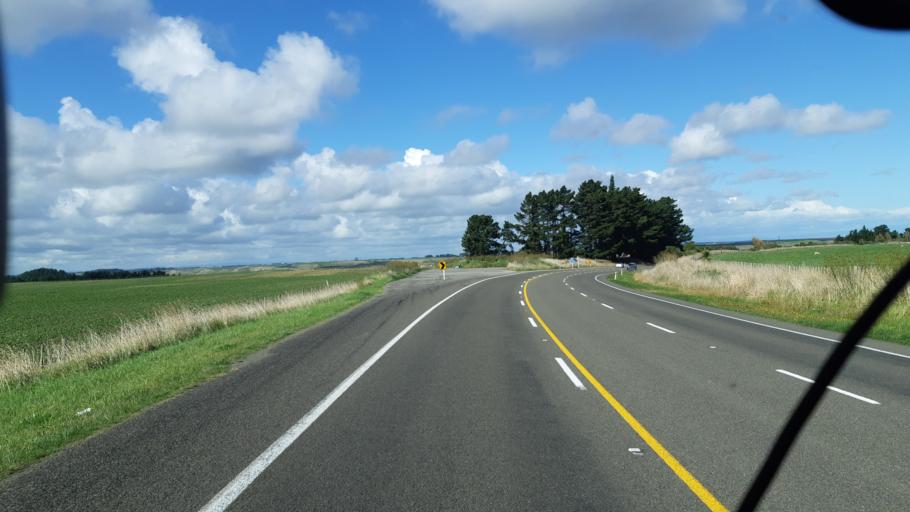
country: NZ
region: Manawatu-Wanganui
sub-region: Wanganui District
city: Wanganui
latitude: -39.9927
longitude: 175.1668
